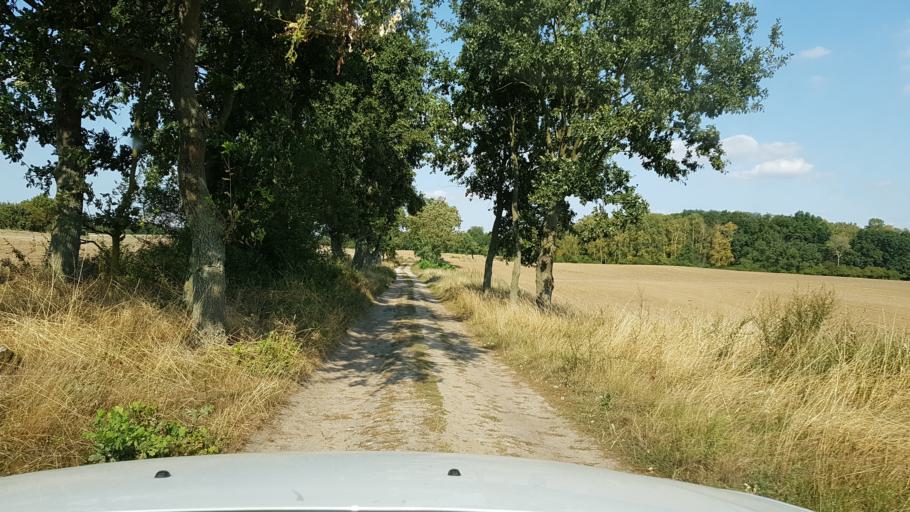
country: PL
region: West Pomeranian Voivodeship
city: Trzcinsko Zdroj
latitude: 52.8975
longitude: 14.5538
